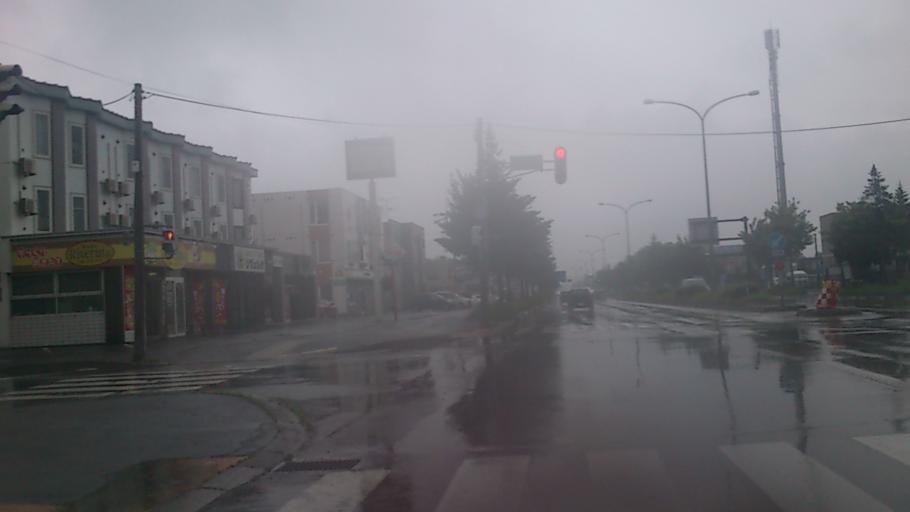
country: JP
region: Hokkaido
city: Obihiro
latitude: 42.9116
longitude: 143.1314
